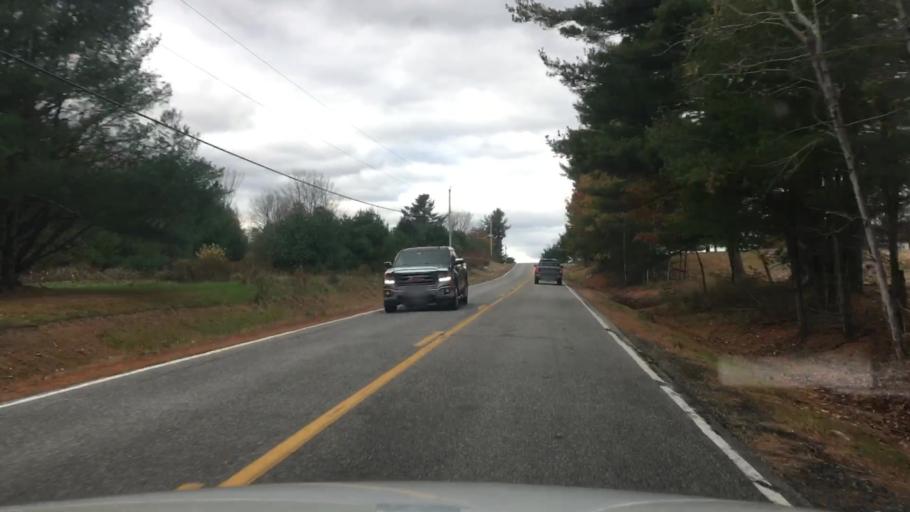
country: US
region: Maine
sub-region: Sagadahoc County
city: Richmond
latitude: 44.1089
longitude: -69.9041
